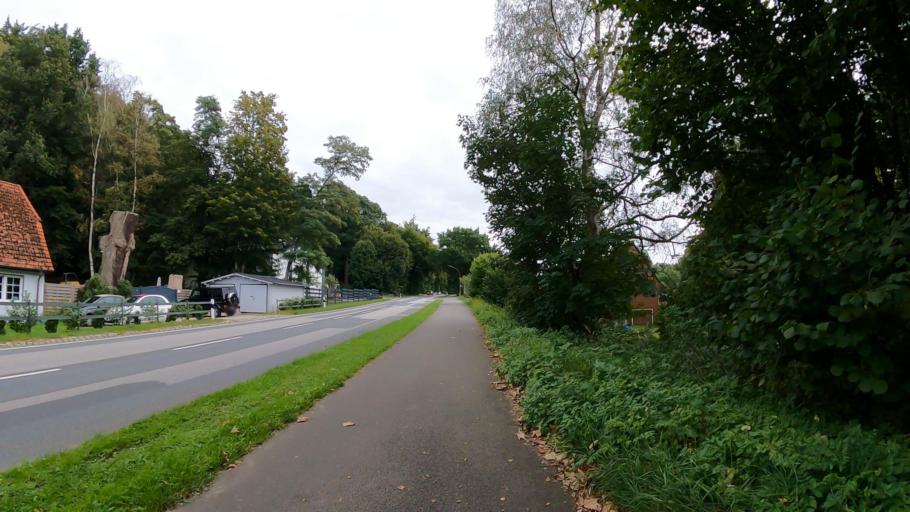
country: DE
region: Schleswig-Holstein
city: Bornsen
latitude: 53.4708
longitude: 10.2698
